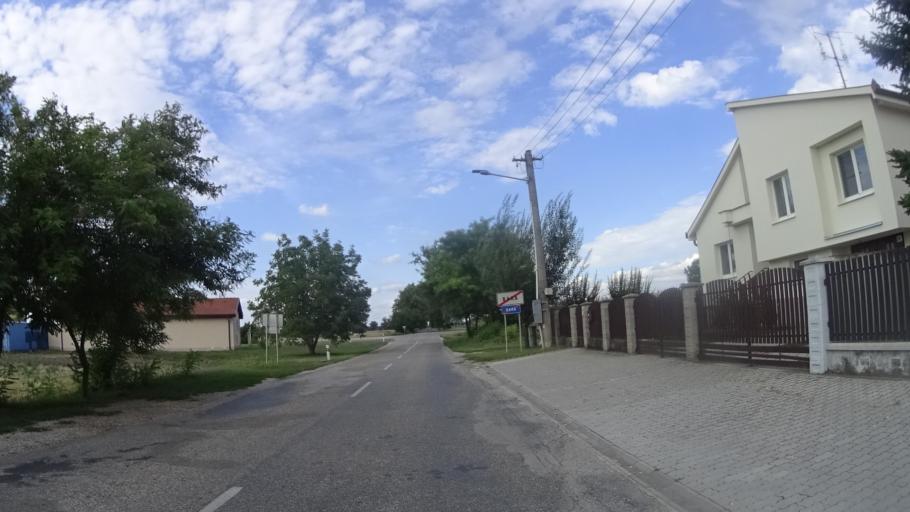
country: SK
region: Trnavsky
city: Gabcikovo
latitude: 47.9102
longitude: 17.5269
